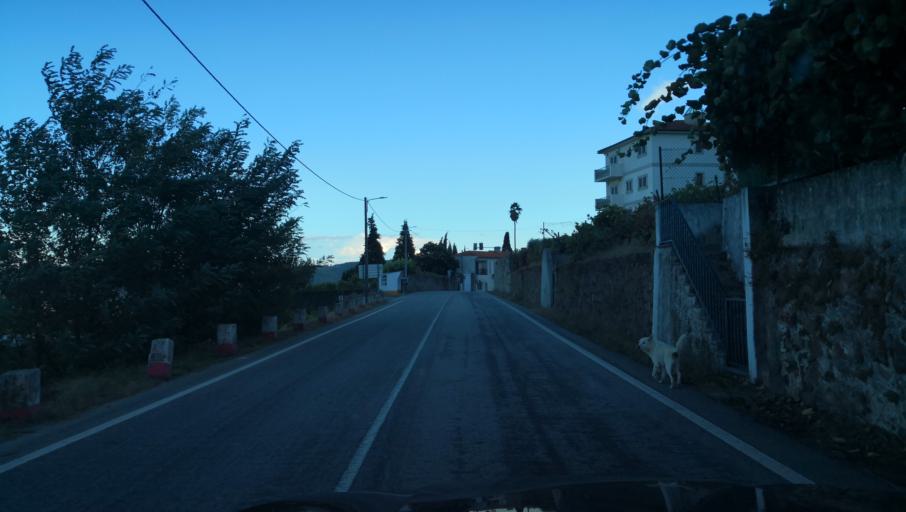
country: PT
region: Vila Real
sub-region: Vila Real
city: Vila Real
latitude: 41.2572
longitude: -7.7714
